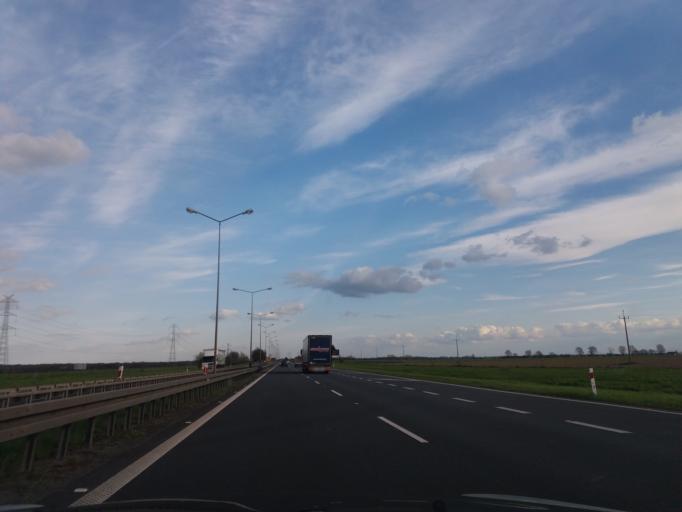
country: PL
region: Lower Silesian Voivodeship
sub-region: Powiat strzelinski
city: Wiazow
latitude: 50.8765
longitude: 17.2054
